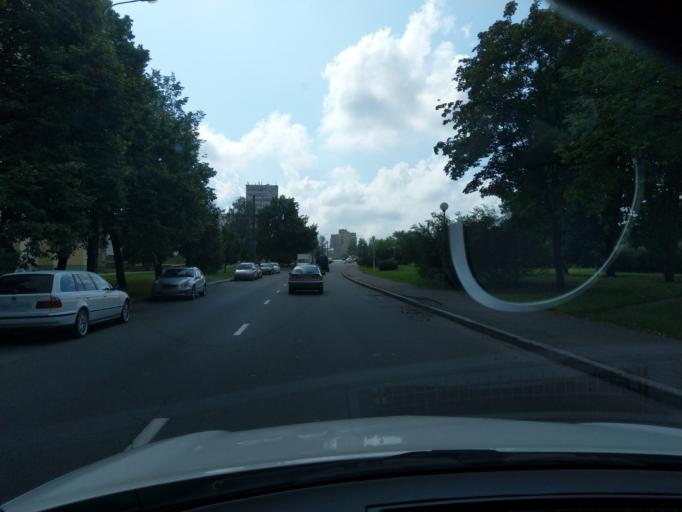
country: BY
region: Minsk
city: Minsk
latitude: 53.8949
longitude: 27.5825
